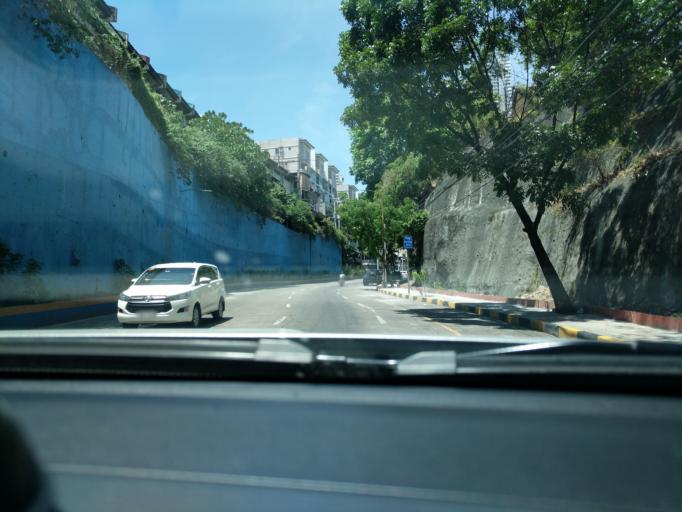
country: PH
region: Metro Manila
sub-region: Pasig
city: Pasig City
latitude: 14.5785
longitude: 121.0680
